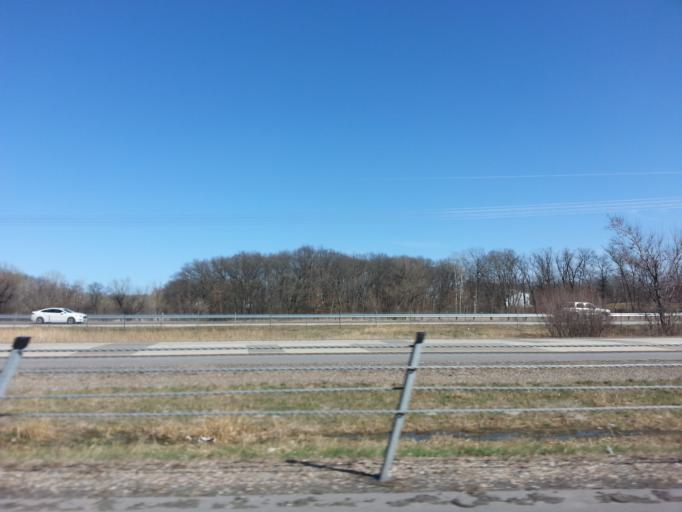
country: US
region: Minnesota
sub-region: Dakota County
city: Lakeville
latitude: 44.6759
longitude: -93.2939
